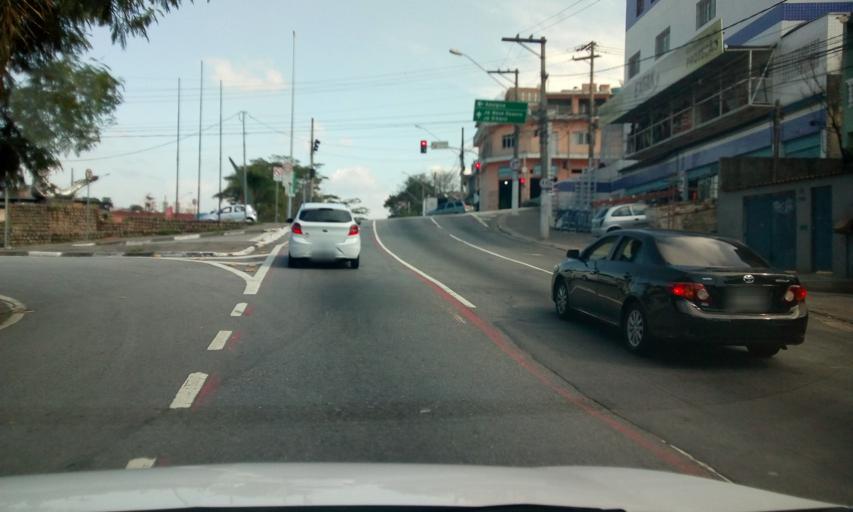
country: BR
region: Sao Paulo
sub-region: Osasco
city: Osasco
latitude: -23.5553
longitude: -46.7811
